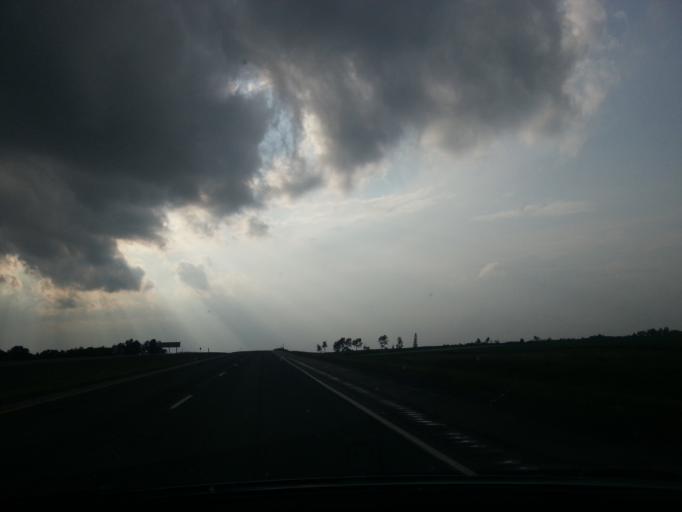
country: CA
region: New Brunswick
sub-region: Madawaska County
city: Saint-Leonard
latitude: 47.1057
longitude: -67.8079
